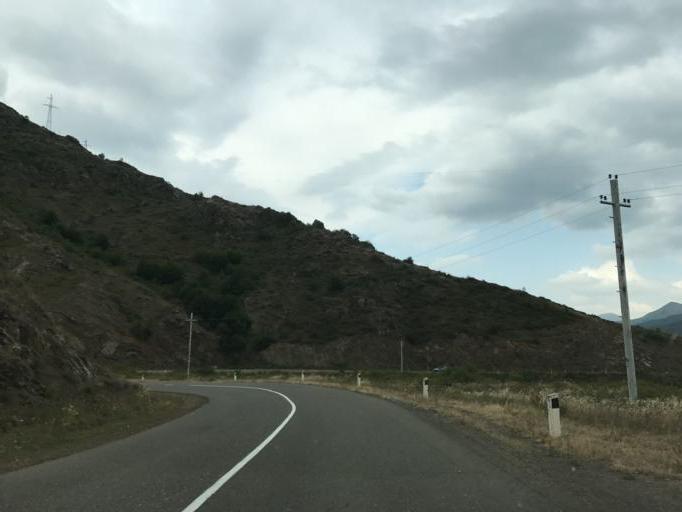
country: AZ
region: Susa
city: Shushi
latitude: 39.7195
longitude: 46.6831
